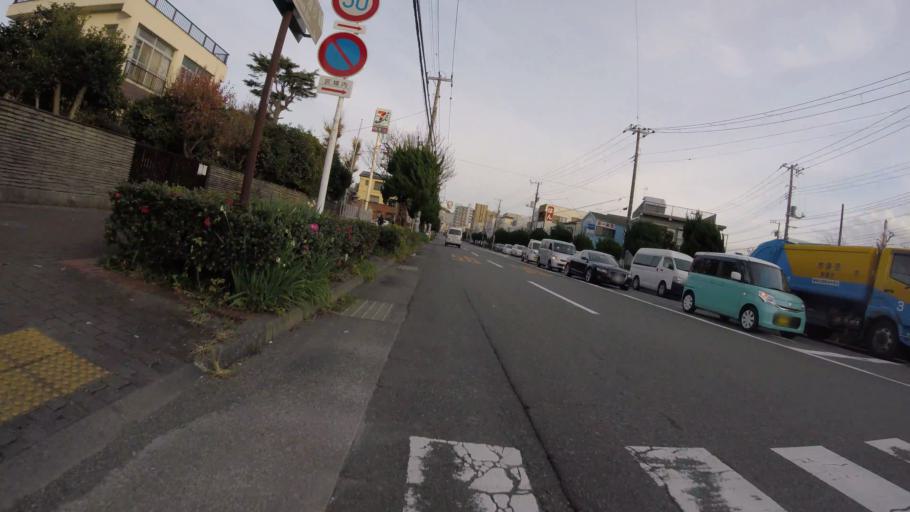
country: JP
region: Shizuoka
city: Numazu
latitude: 35.0979
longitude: 138.8502
